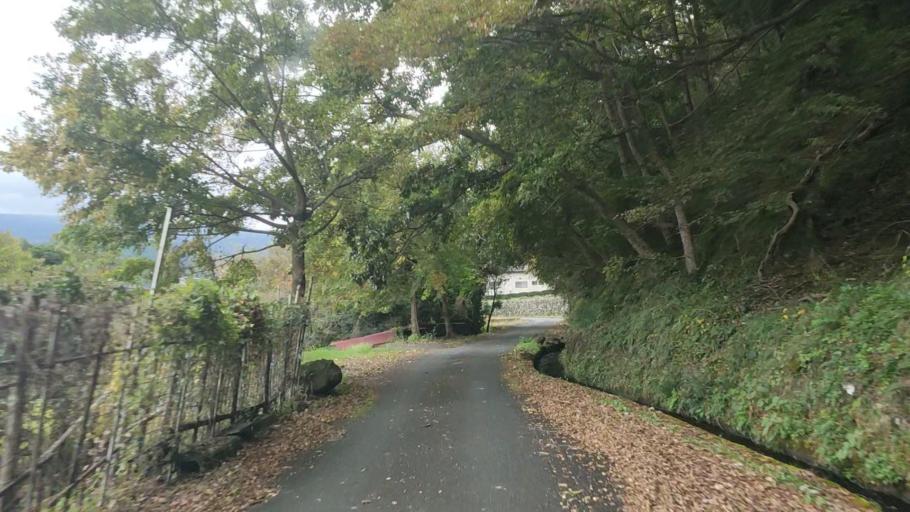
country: JP
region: Shizuoka
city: Ito
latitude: 34.9331
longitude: 138.9916
